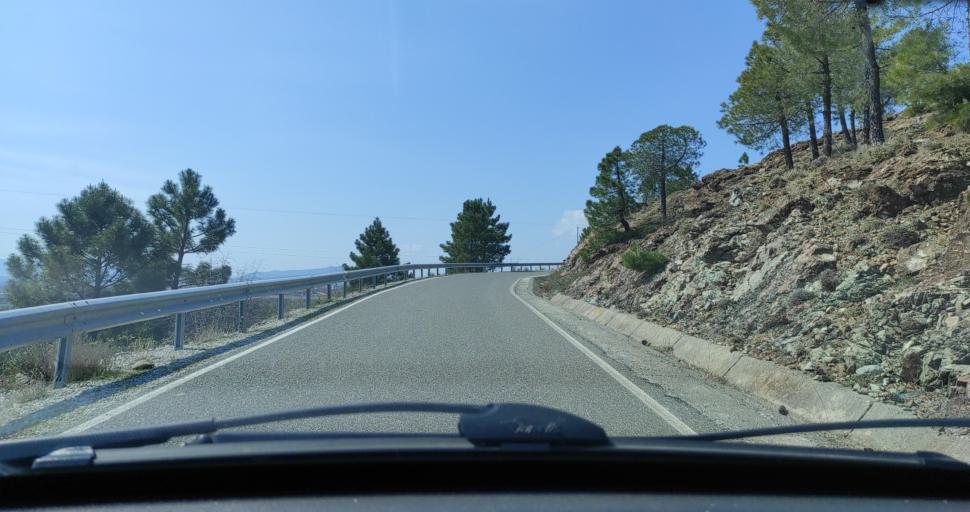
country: AL
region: Shkoder
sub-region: Rrethi i Shkodres
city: Hajmel
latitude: 41.9824
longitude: 19.6454
